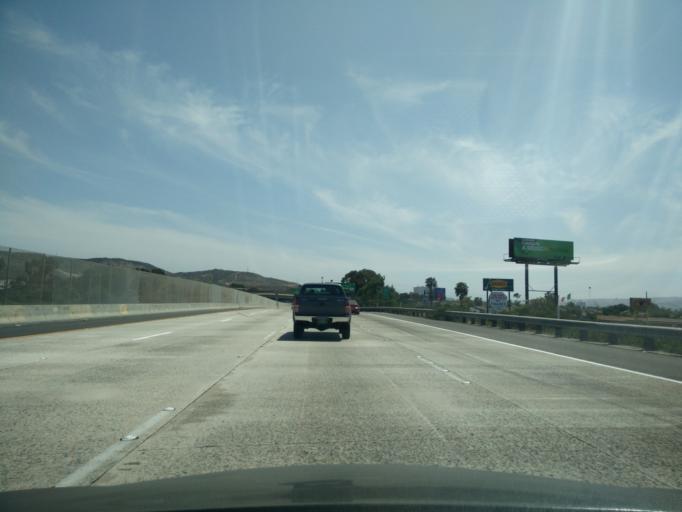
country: MX
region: Baja California
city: Tijuana
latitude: 32.5513
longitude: -117.0454
